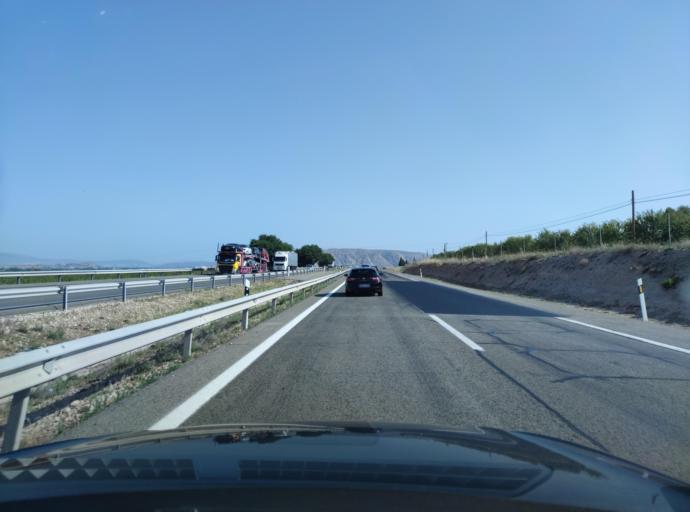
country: ES
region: Valencia
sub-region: Provincia de Alicante
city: Villena
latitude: 38.5867
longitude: -0.8436
